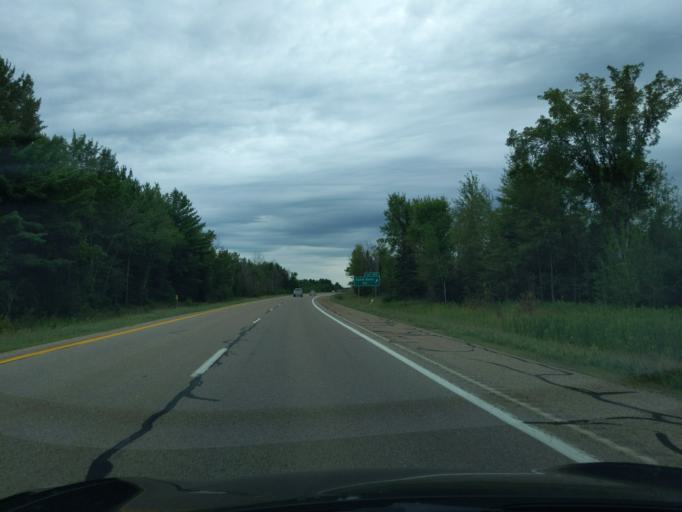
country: US
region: Michigan
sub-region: Roscommon County
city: Houghton Lake
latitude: 44.2774
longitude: -84.8004
